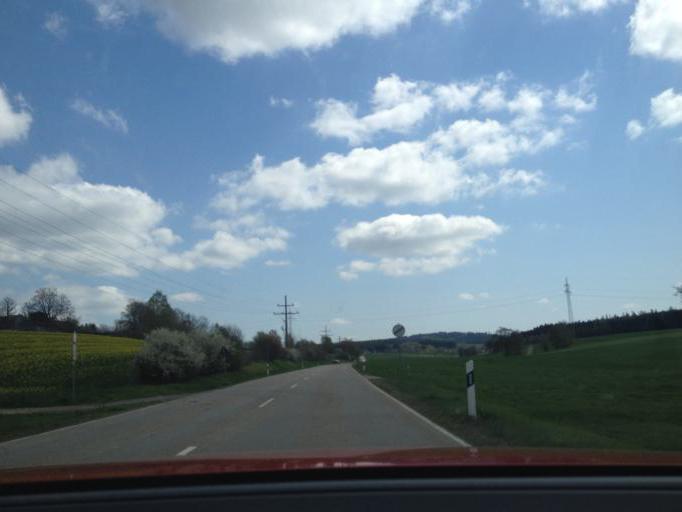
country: DE
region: Bavaria
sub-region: Upper Palatinate
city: Waldershof
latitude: 49.9838
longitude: 12.0776
